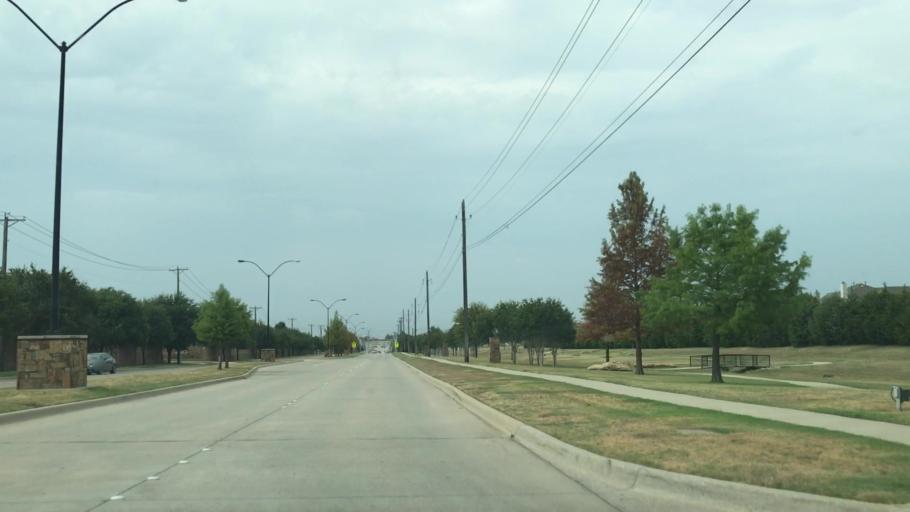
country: US
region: Texas
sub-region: Tarrant County
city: Keller
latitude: 32.9053
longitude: -97.2727
